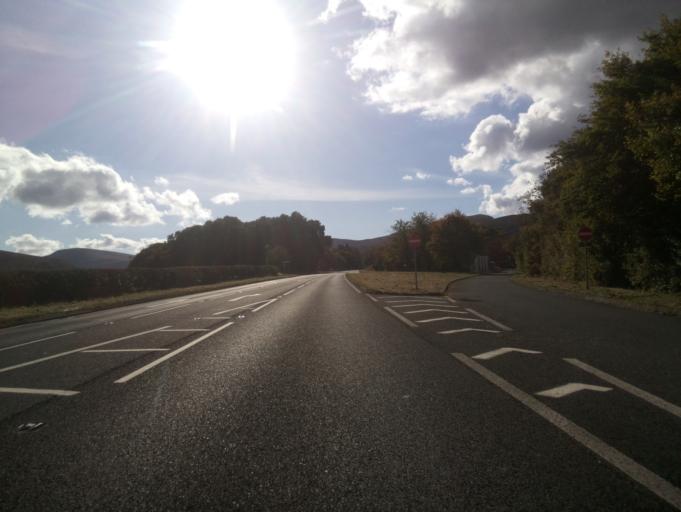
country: GB
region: Wales
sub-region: Sir Powys
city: Brecon
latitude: 51.9128
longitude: -3.4726
